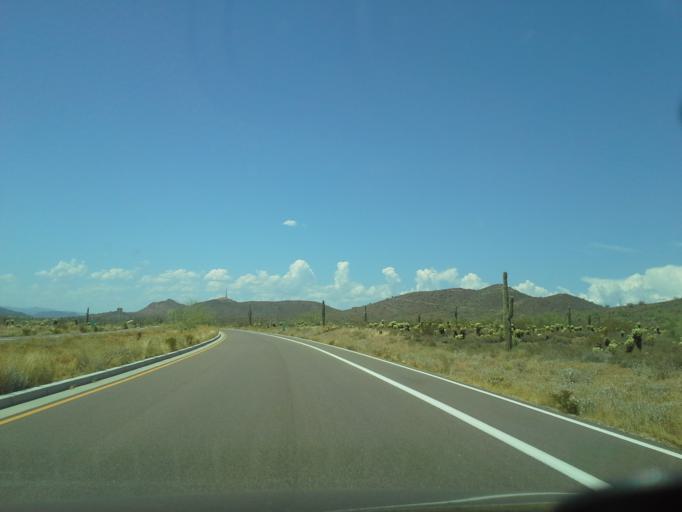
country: US
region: Arizona
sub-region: Maricopa County
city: Cave Creek
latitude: 33.7709
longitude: -112.0617
